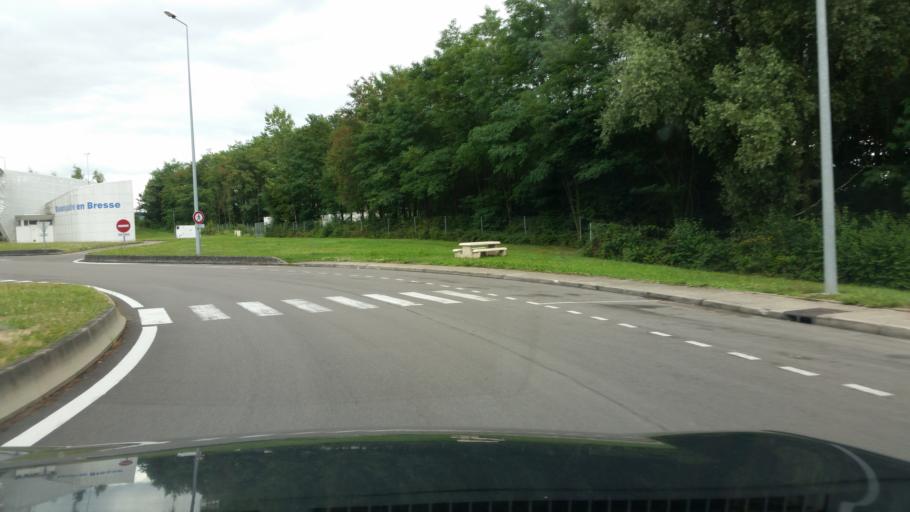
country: FR
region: Franche-Comte
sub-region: Departement du Jura
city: Bletterans
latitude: 46.6666
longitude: 5.4177
